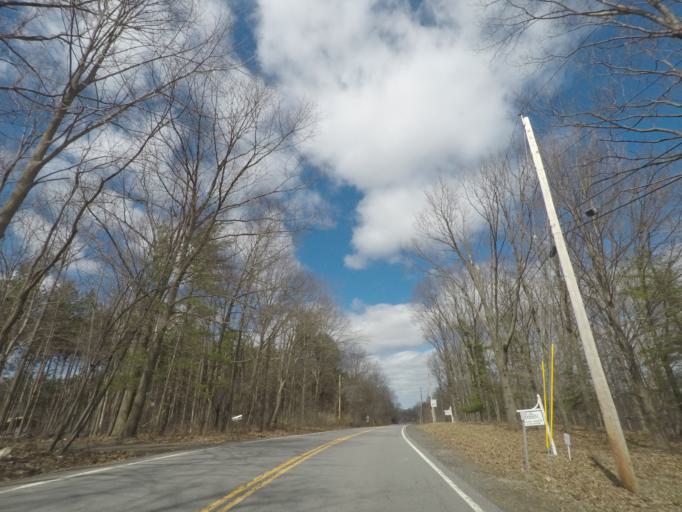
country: US
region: New York
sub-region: Albany County
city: Voorheesville
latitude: 42.6348
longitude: -73.9701
